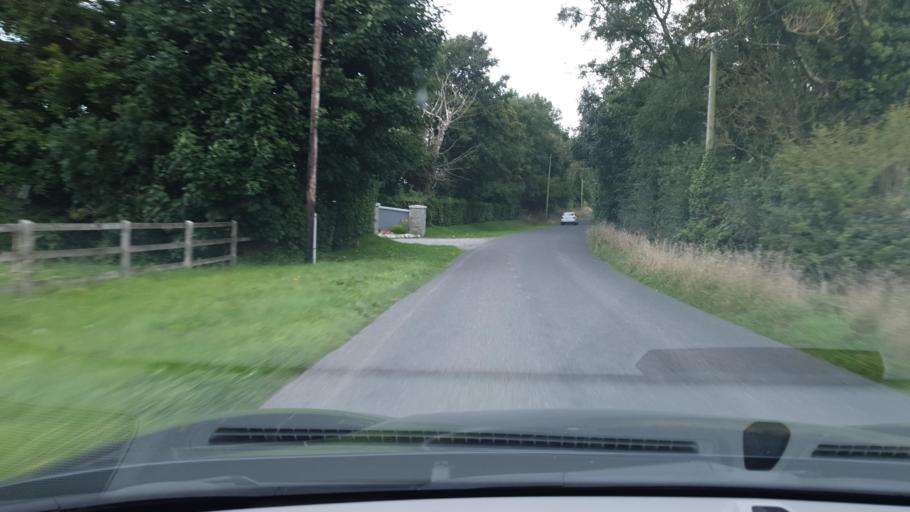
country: IE
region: Leinster
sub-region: An Mhi
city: Dunshaughlin
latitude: 53.5481
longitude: -6.5354
